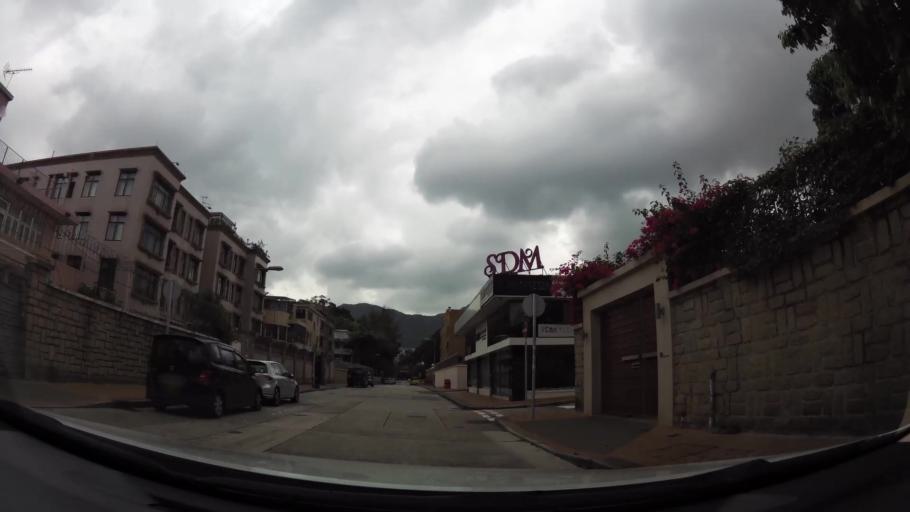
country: HK
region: Kowloon City
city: Kowloon
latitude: 22.3309
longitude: 114.1795
